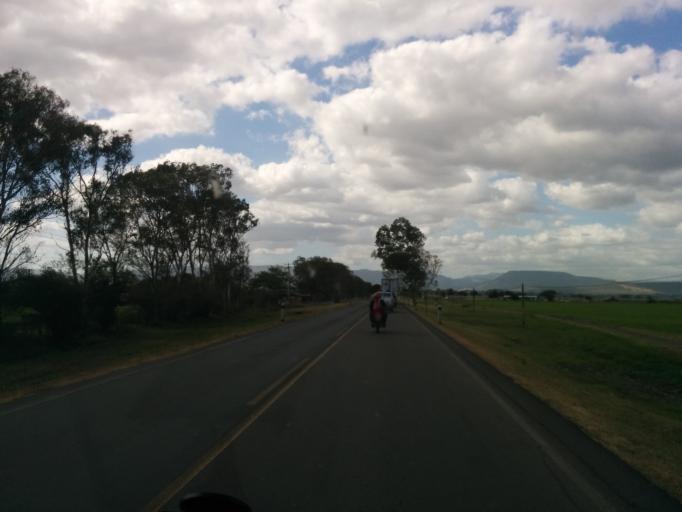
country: NI
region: Matagalpa
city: Ciudad Dario
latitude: 12.8657
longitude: -86.1156
